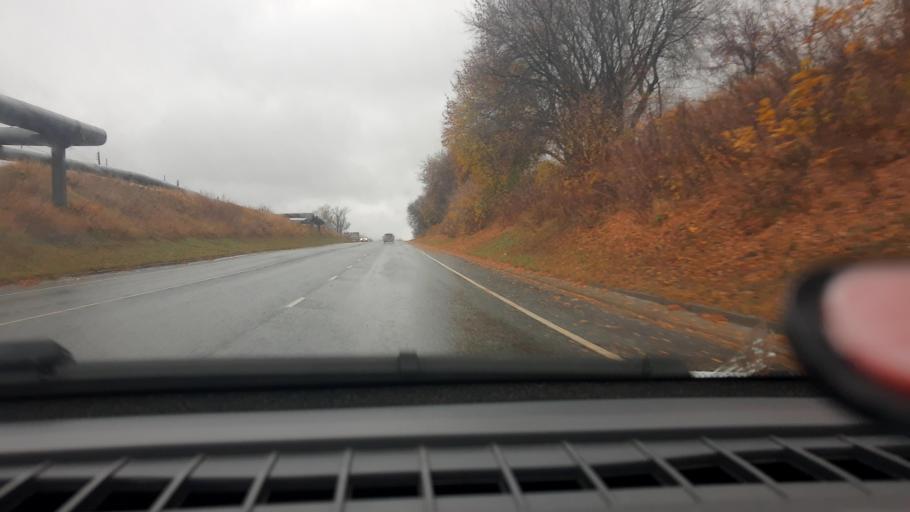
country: RU
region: Nizjnij Novgorod
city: Kstovo
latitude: 56.1340
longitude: 44.1786
